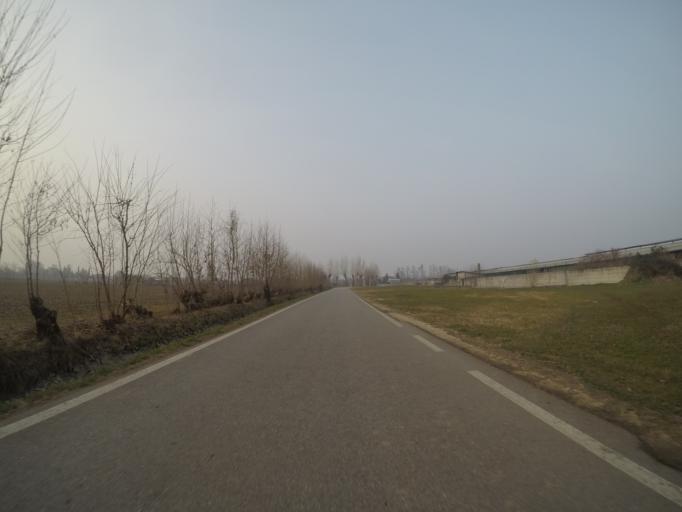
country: IT
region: Veneto
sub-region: Provincia di Treviso
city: Altivole
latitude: 45.7443
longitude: 11.9586
